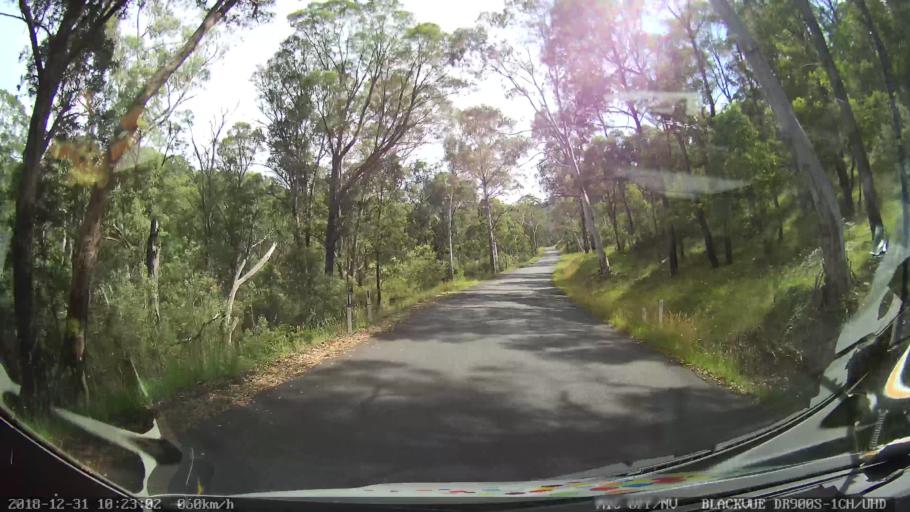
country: AU
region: New South Wales
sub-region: Snowy River
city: Jindabyne
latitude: -36.5204
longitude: 148.1431
